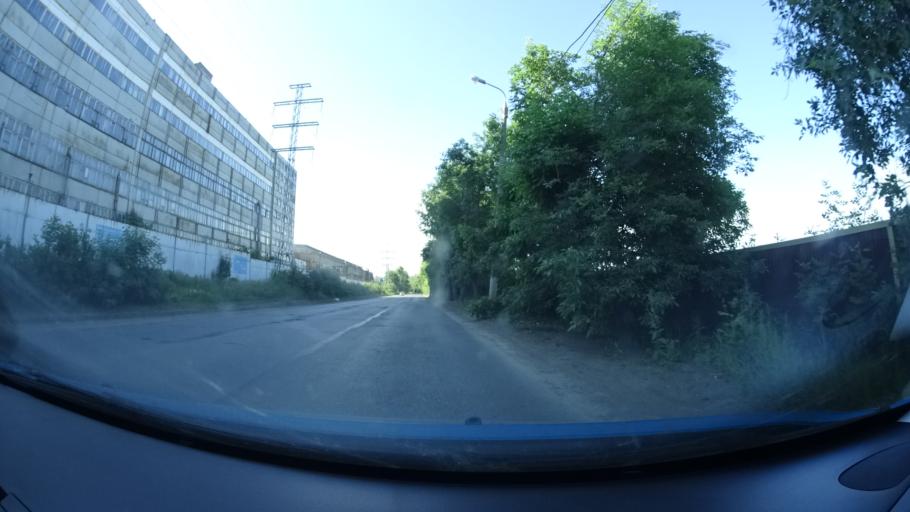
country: RU
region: Bashkortostan
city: Ufa
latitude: 54.8416
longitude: 56.0755
